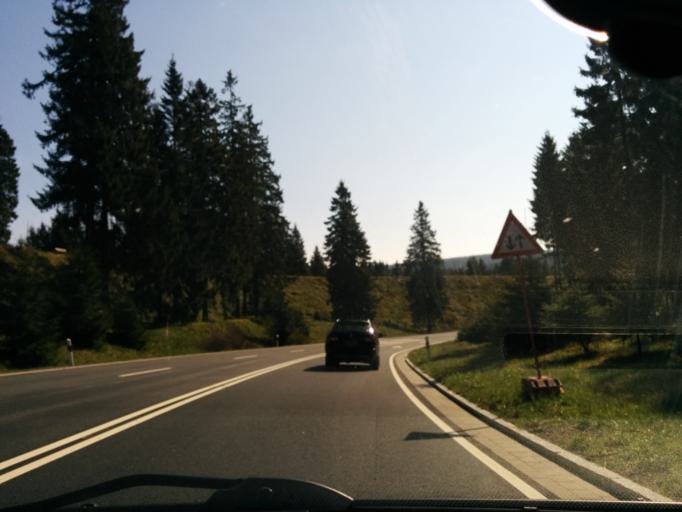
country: DE
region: Lower Saxony
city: Altenau
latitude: 51.7820
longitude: 10.4153
